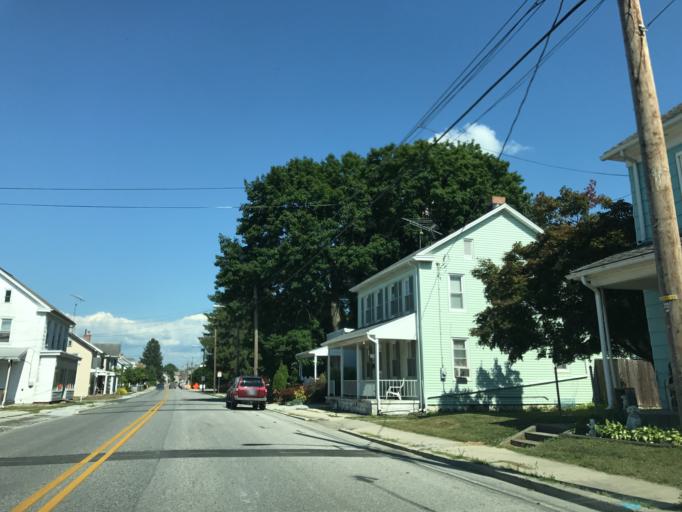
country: US
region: Pennsylvania
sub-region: Adams County
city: Midway
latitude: 39.8049
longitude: -77.0036
